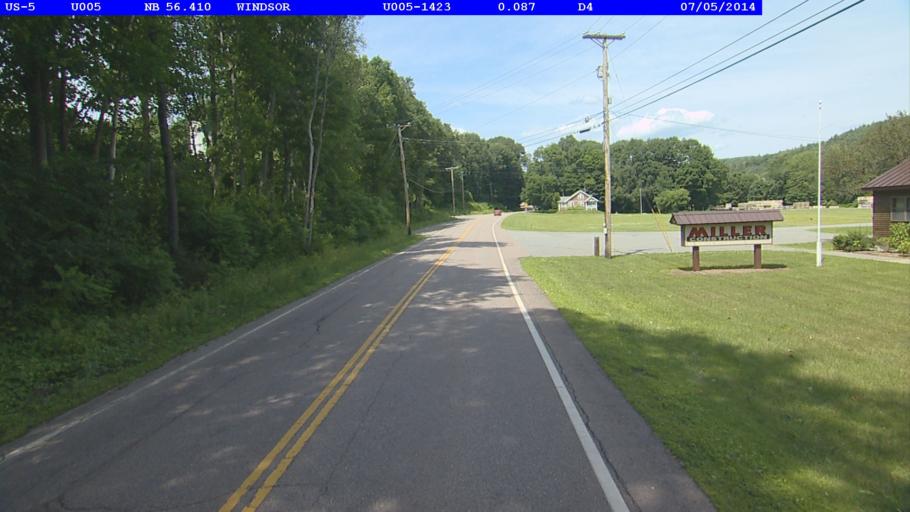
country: US
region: Vermont
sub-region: Windsor County
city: Windsor
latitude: 43.4303
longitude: -72.3985
